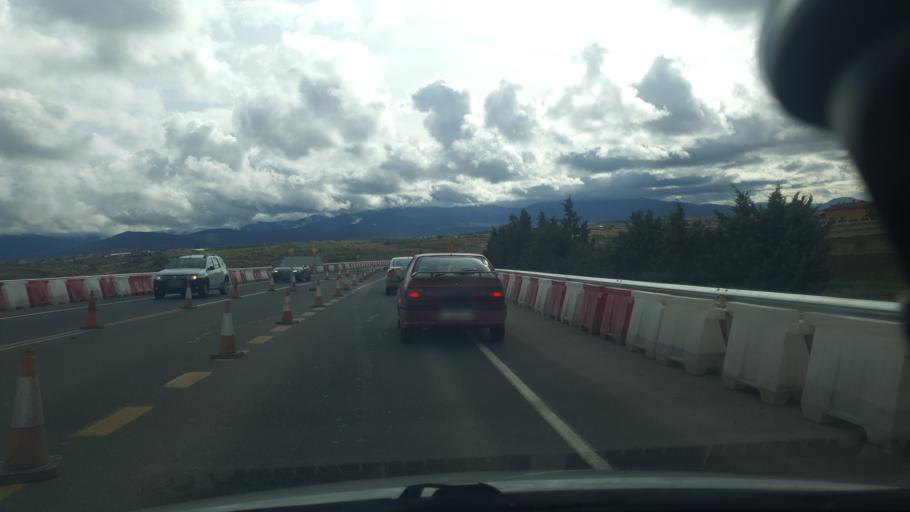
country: ES
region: Castille and Leon
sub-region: Provincia de Segovia
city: San Cristobal de Segovia
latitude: 40.9694
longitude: -4.0854
